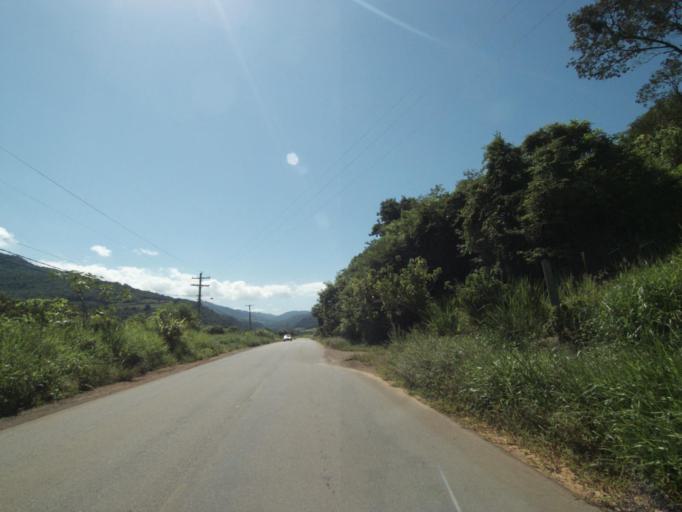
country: BR
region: Rio Grande do Sul
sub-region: Bento Goncalves
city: Bento Goncalves
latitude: -29.0900
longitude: -51.6406
